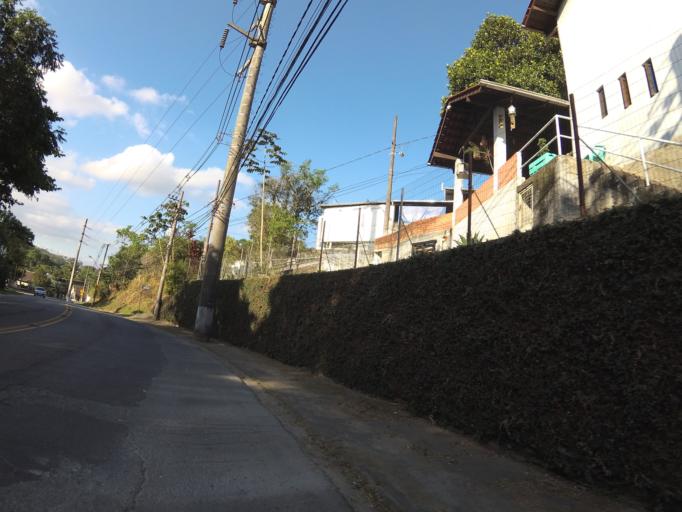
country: BR
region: Santa Catarina
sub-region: Blumenau
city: Blumenau
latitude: -26.9252
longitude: -49.1087
